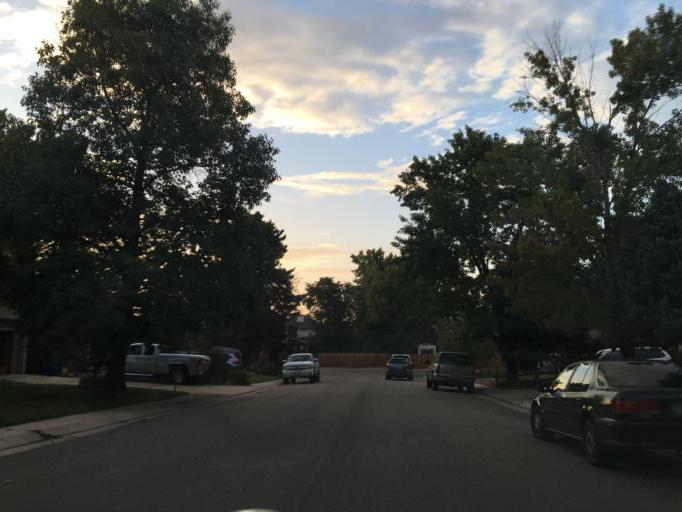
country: US
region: Colorado
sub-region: Adams County
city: Aurora
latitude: 39.6884
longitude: -104.8600
